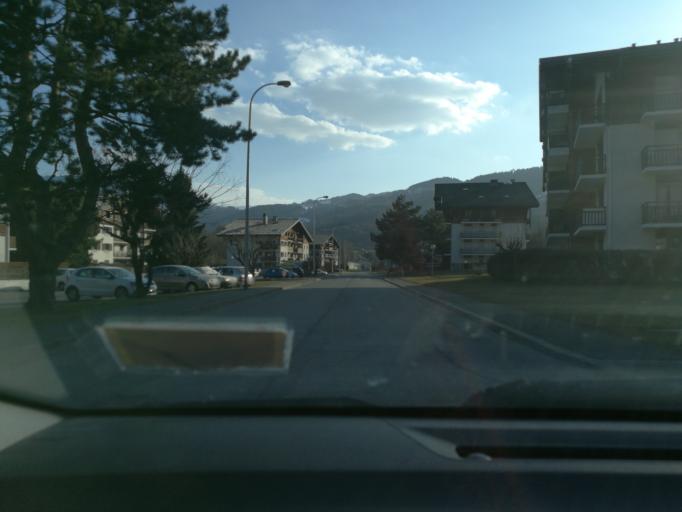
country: FR
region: Rhone-Alpes
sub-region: Departement de la Haute-Savoie
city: Sallanches
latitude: 45.9357
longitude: 6.6388
